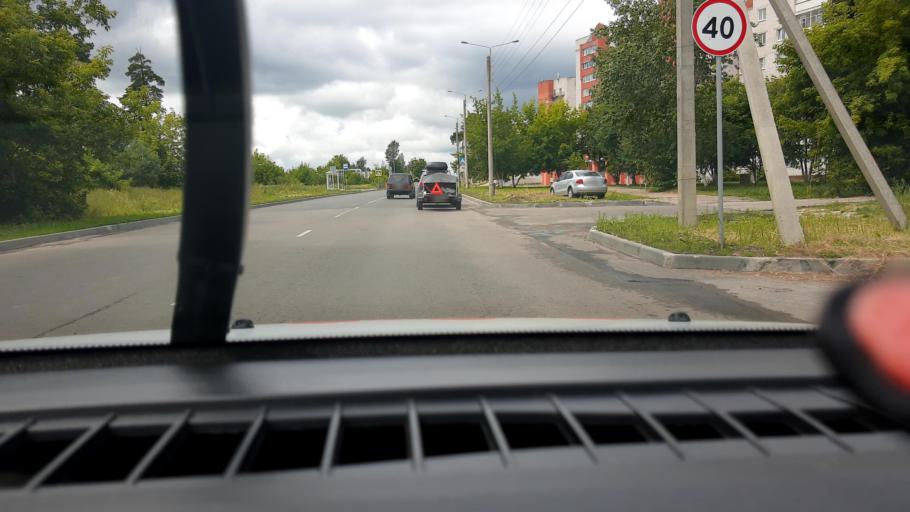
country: RU
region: Nizjnij Novgorod
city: Dzerzhinsk
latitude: 56.2217
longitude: 43.4118
